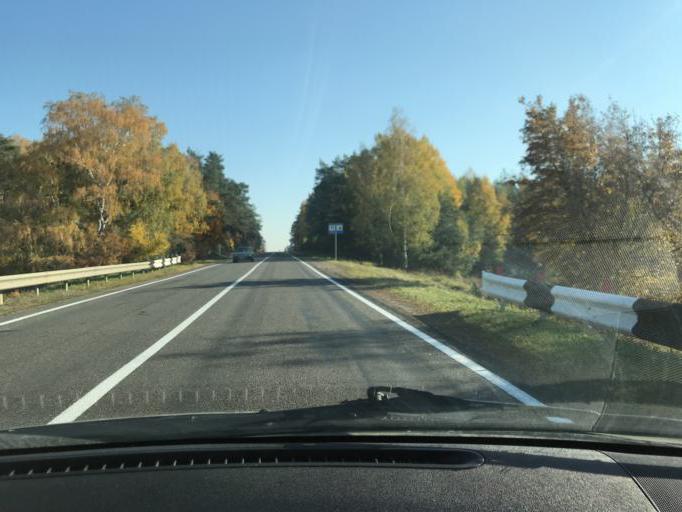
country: BY
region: Minsk
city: Klyetsk
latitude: 52.9689
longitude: 26.6128
